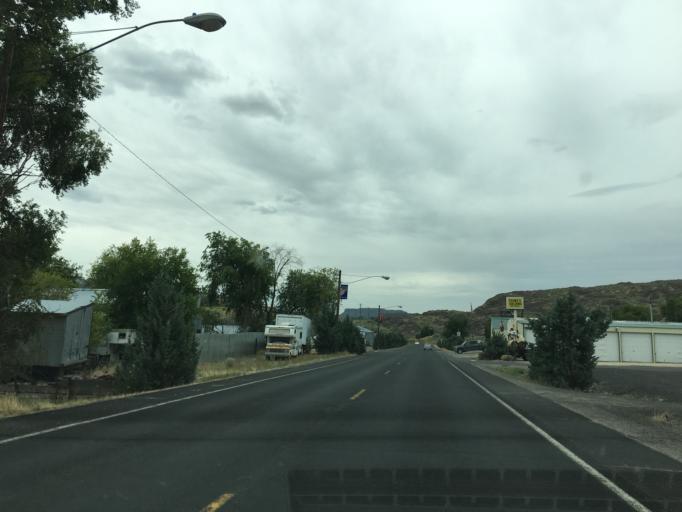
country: US
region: Washington
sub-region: Okanogan County
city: Coulee Dam
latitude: 47.9310
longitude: -119.0408
